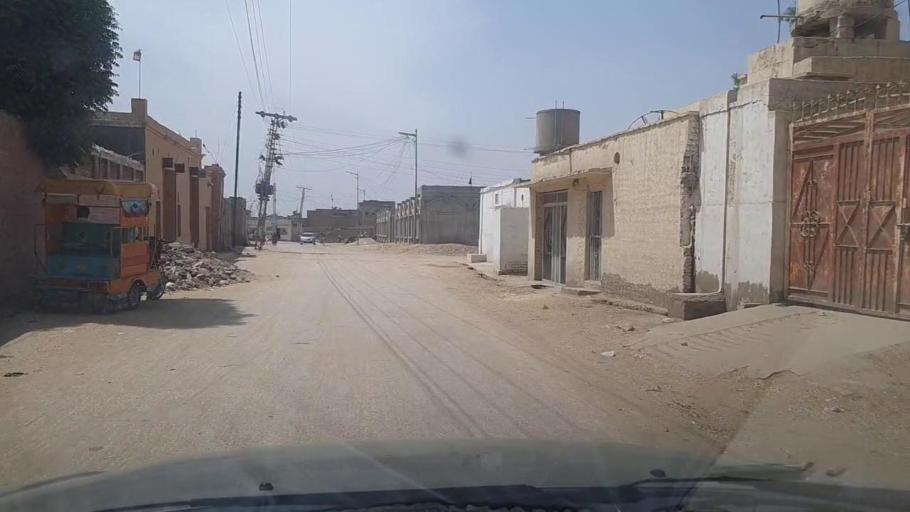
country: PK
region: Sindh
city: Bhiria
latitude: 26.9083
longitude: 68.1920
